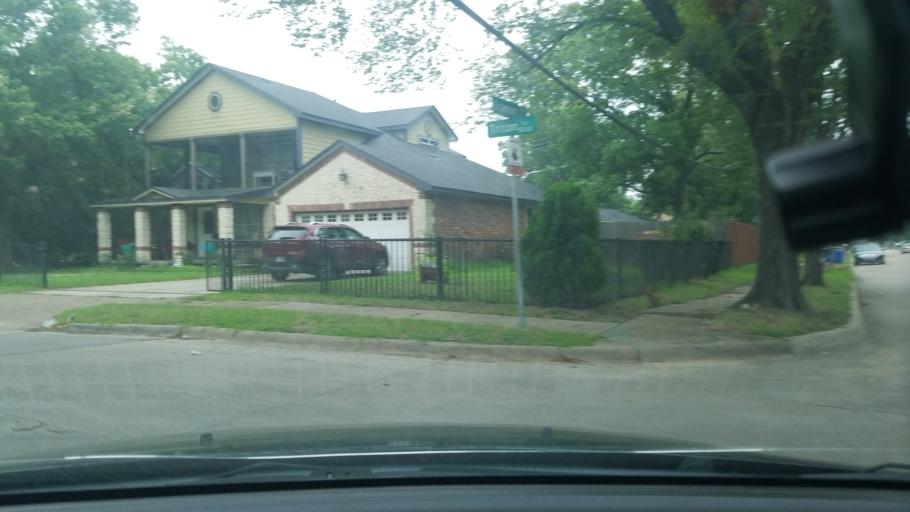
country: US
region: Texas
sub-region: Dallas County
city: Balch Springs
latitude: 32.7538
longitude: -96.6772
